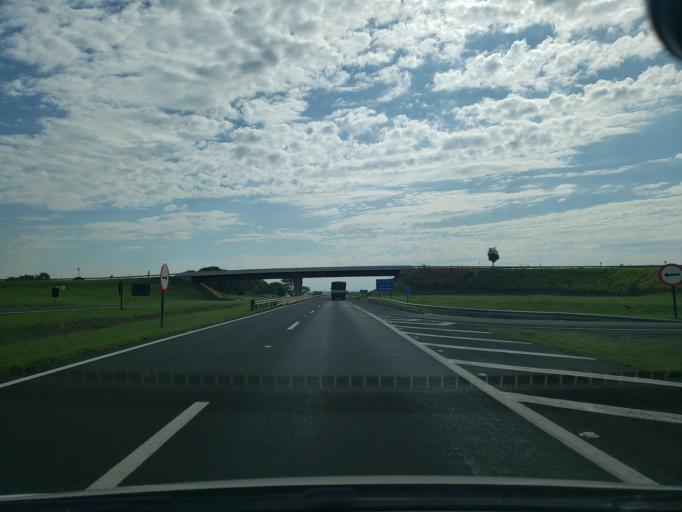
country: BR
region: Sao Paulo
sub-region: Promissao
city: Promissao
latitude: -21.6316
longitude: -49.8390
